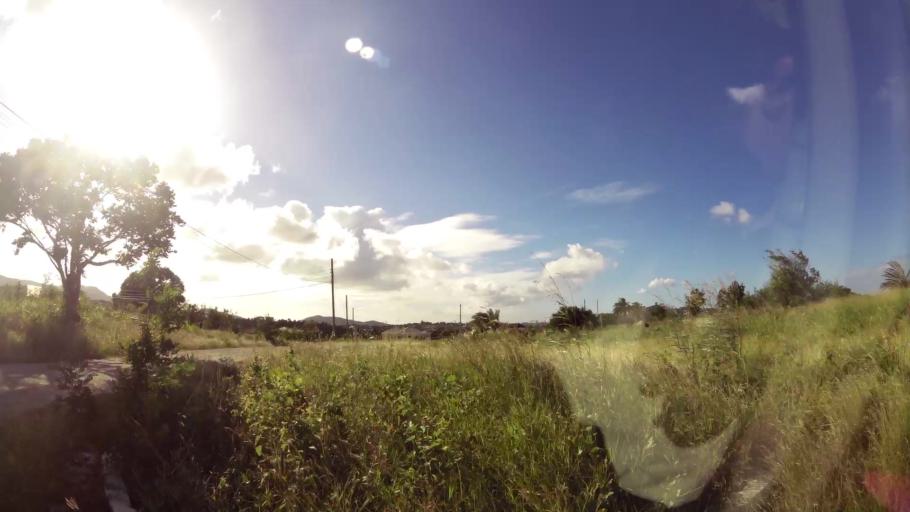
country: AG
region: Saint John
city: Potters Village
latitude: 17.0927
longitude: -61.8039
